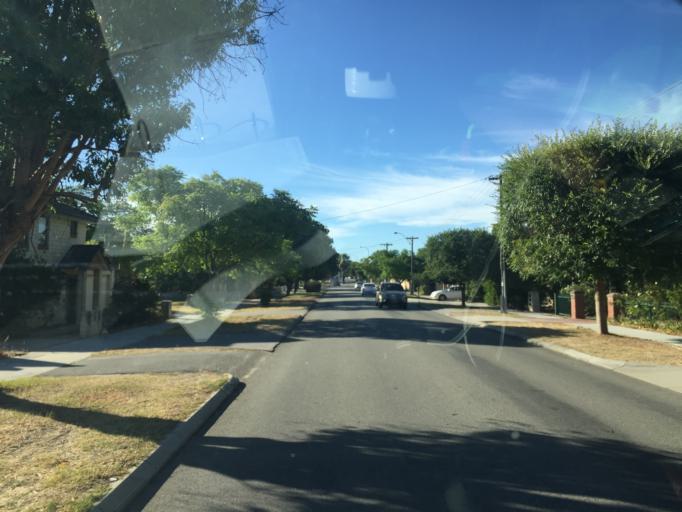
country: AU
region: Western Australia
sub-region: Belmont
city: Rivervale
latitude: -31.9647
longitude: 115.9172
